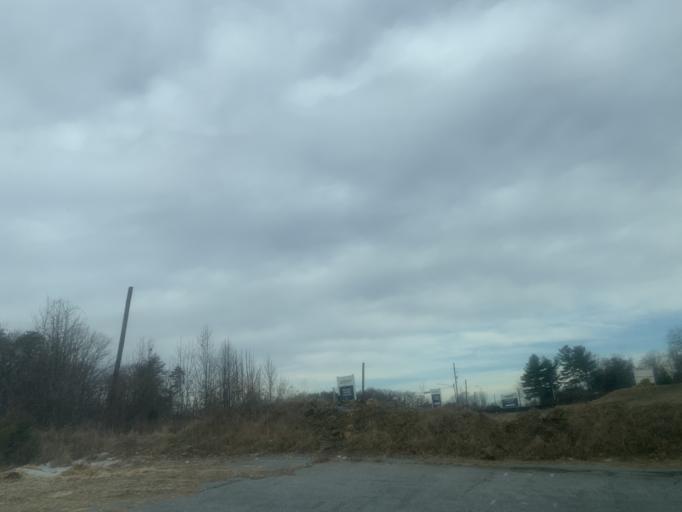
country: US
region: Maryland
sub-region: Prince George's County
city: Forestville
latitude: 38.8287
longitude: -76.8550
